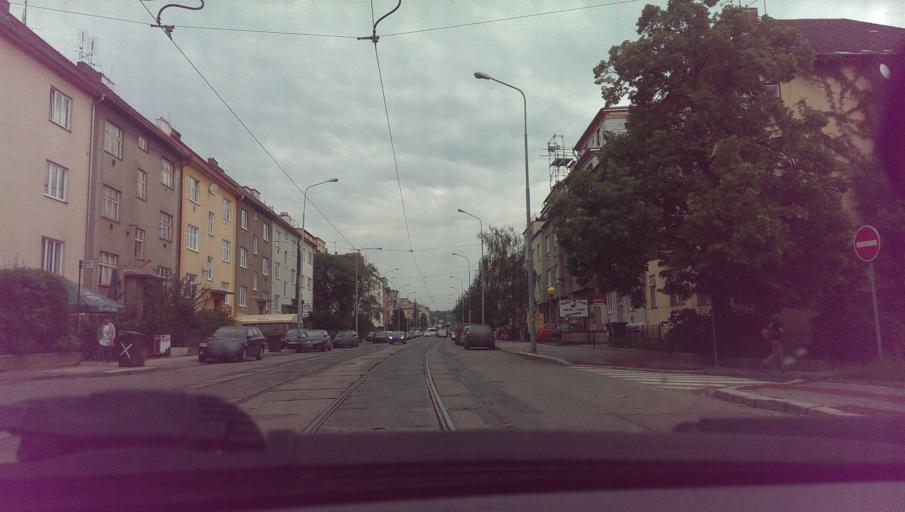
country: CZ
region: South Moravian
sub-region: Mesto Brno
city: Brno
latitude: 49.2102
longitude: 16.6240
